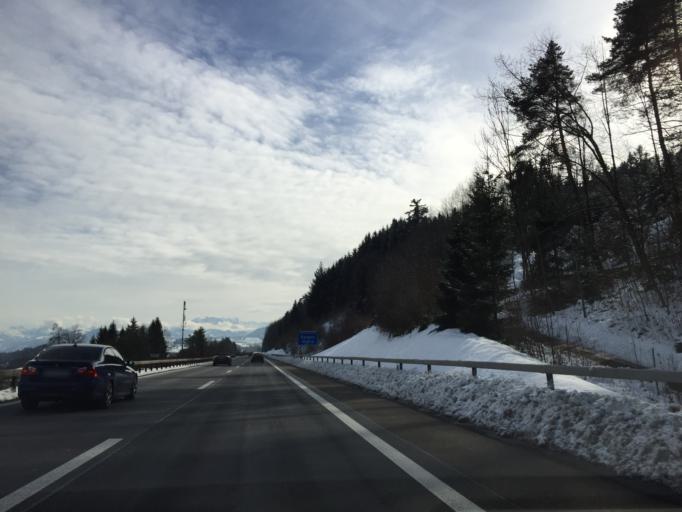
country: CH
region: Zurich
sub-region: Bezirk Horgen
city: Horgen / Oberdorf
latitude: 47.2497
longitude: 8.5955
